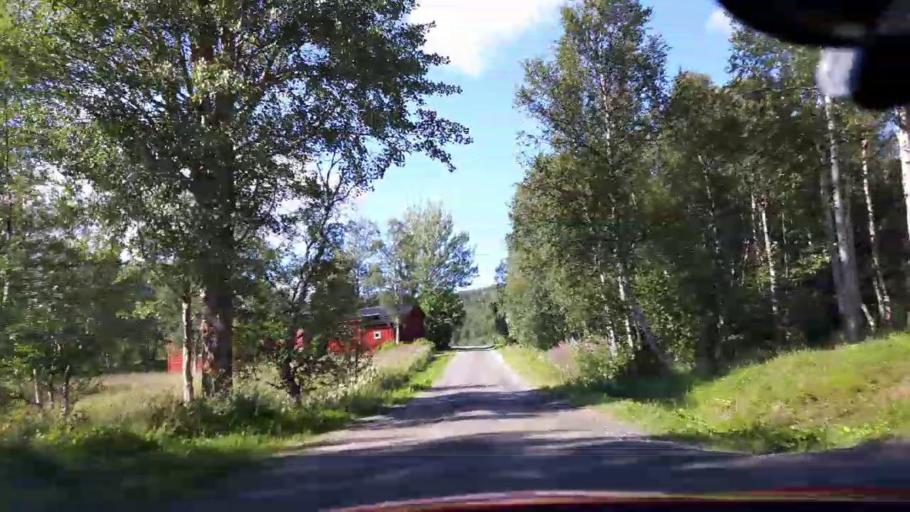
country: SE
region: Jaemtland
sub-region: Are Kommun
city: Are
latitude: 63.2109
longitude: 13.0546
